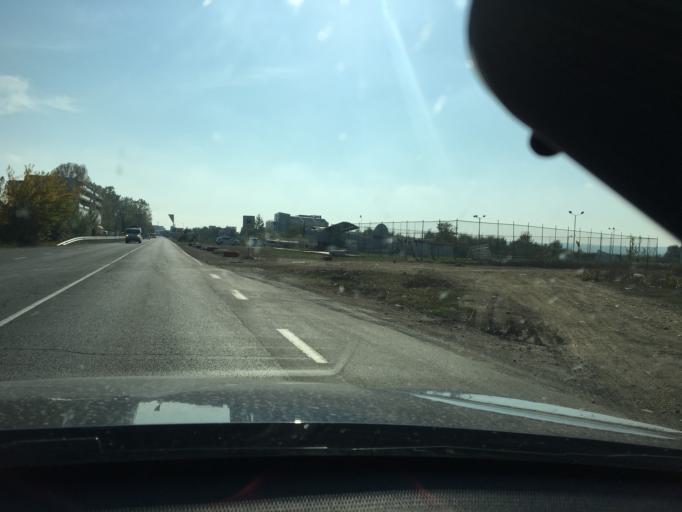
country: BG
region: Burgas
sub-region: Obshtina Nesebur
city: Nesebar
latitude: 42.6967
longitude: 27.7026
